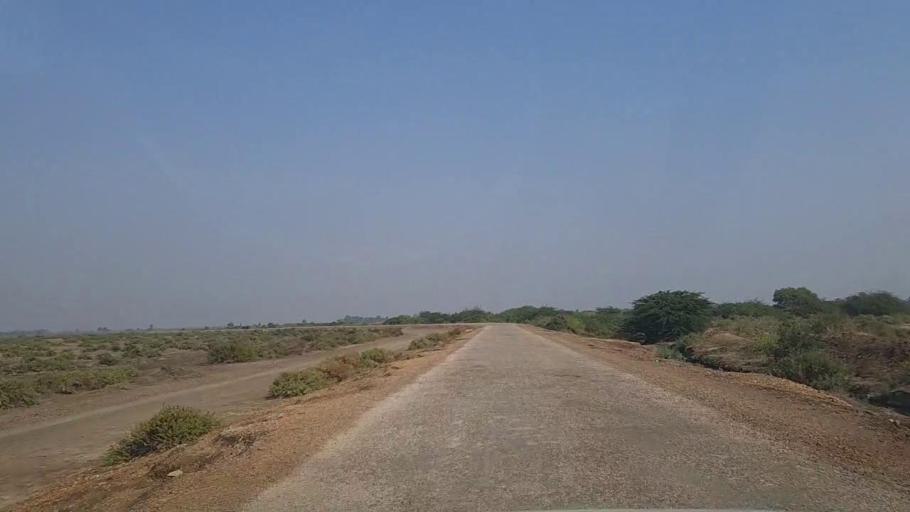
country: PK
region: Sindh
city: Keti Bandar
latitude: 24.2408
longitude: 67.6912
